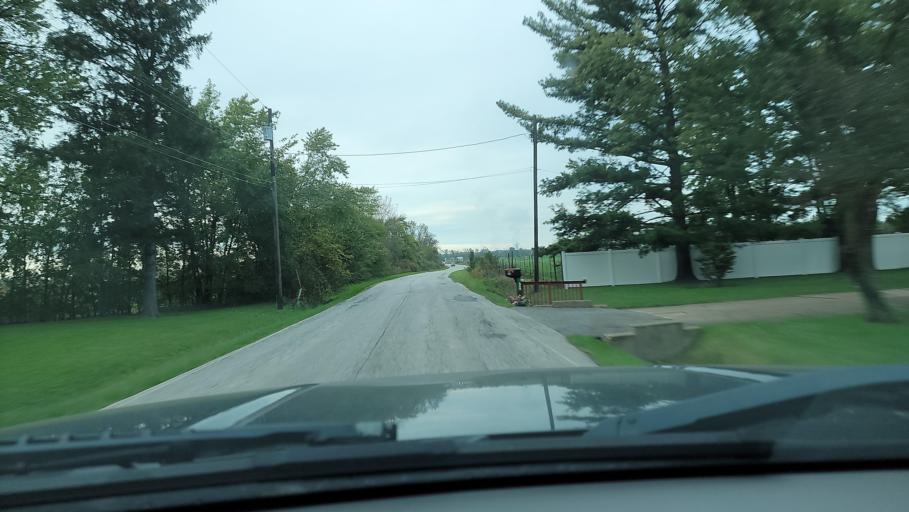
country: US
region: Indiana
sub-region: Porter County
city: South Haven
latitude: 41.5575
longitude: -87.1532
